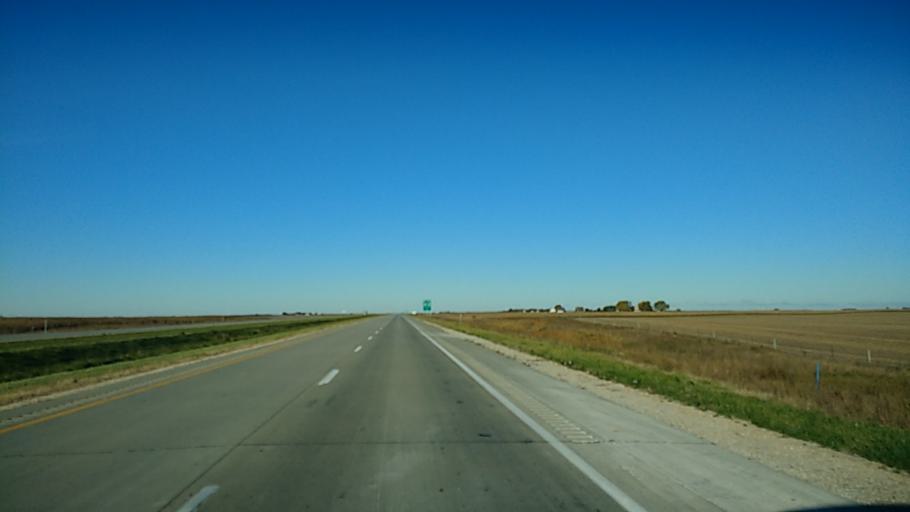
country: US
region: Iowa
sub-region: Sac County
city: Sac City
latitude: 42.4542
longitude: -94.9205
